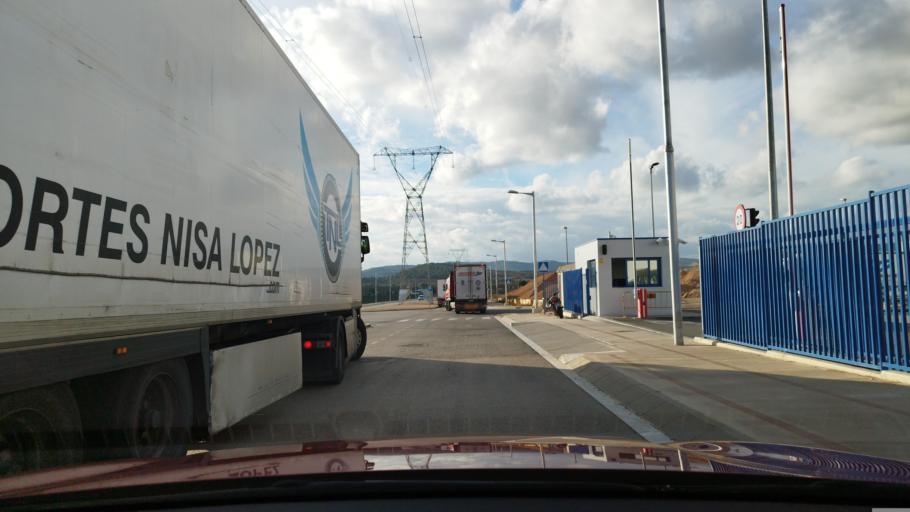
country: ES
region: Catalonia
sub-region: Provincia de Tarragona
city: la Bisbal del Penedes
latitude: 41.2759
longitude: 1.5077
